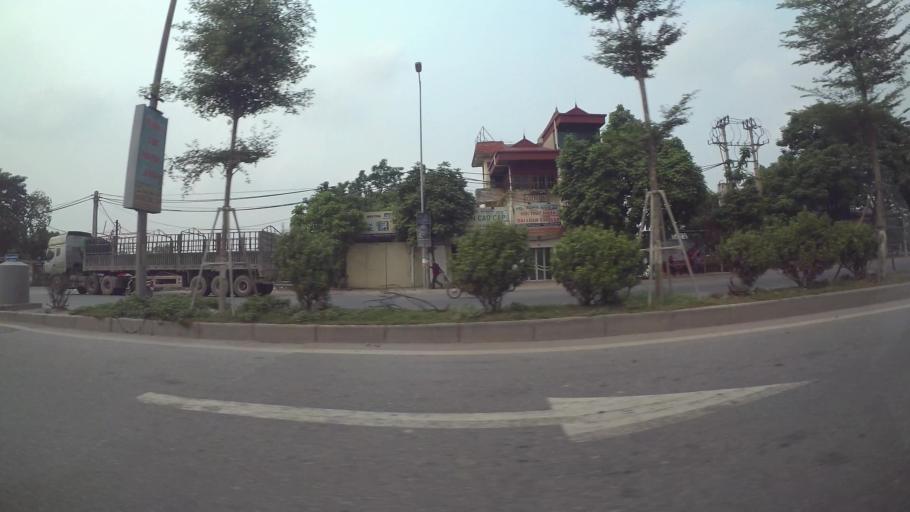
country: VN
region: Ha Noi
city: Trau Quy
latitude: 21.0269
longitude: 105.9238
